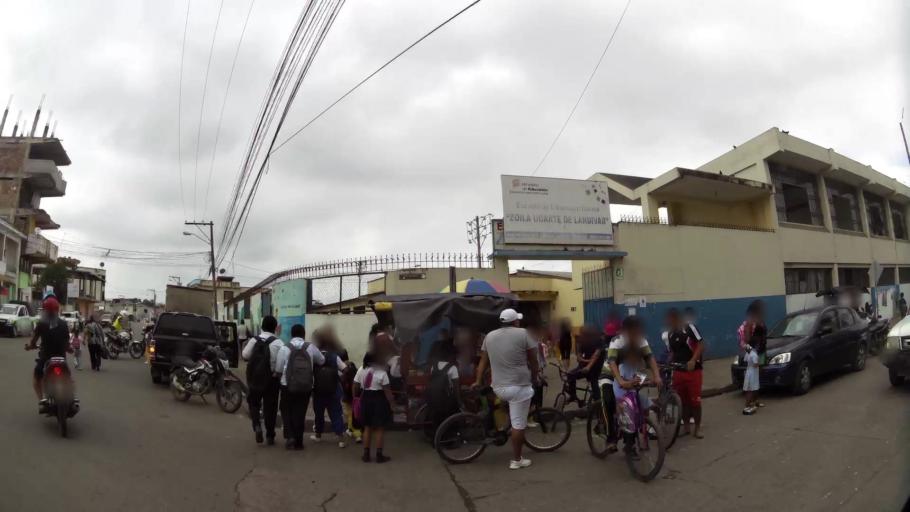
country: EC
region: El Oro
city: Pasaje
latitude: -3.2452
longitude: -79.8336
